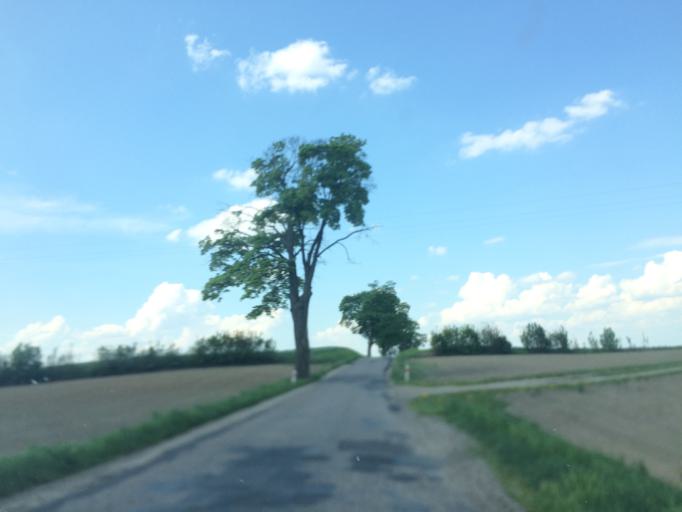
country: PL
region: Warmian-Masurian Voivodeship
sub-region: Powiat ilawski
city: Lubawa
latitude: 53.4088
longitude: 19.7859
